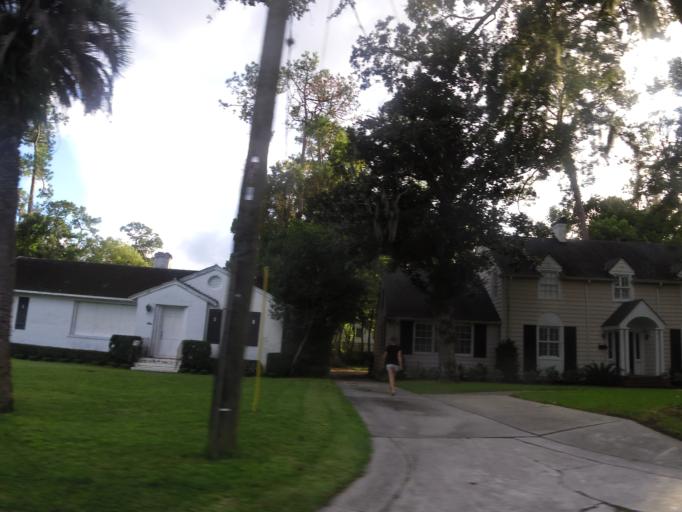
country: US
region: Florida
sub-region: Duval County
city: Jacksonville
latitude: 30.2861
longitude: -81.6516
